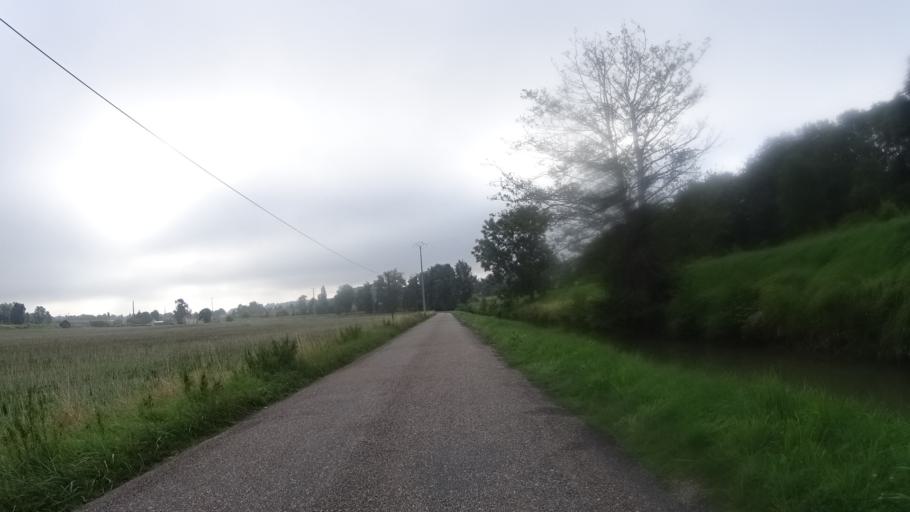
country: FR
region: Lorraine
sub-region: Departement de la Meuse
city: Fains-Veel
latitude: 48.8029
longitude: 5.0604
